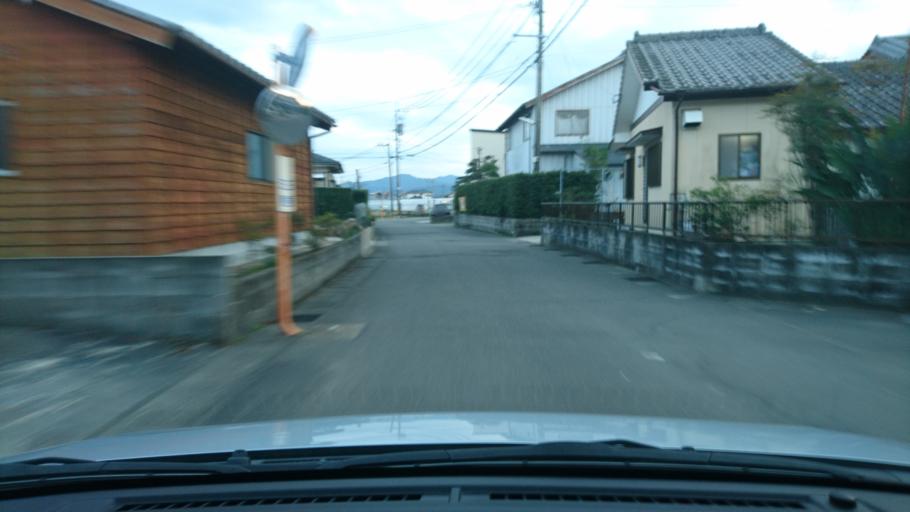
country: JP
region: Miyazaki
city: Miyazaki-shi
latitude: 31.8508
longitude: 131.4322
